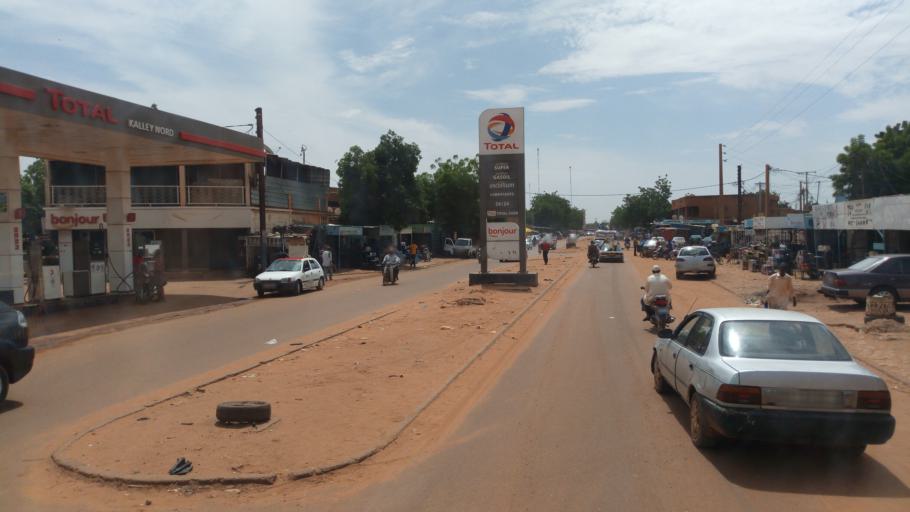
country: NE
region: Niamey
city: Niamey
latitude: 13.5182
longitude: 2.1259
